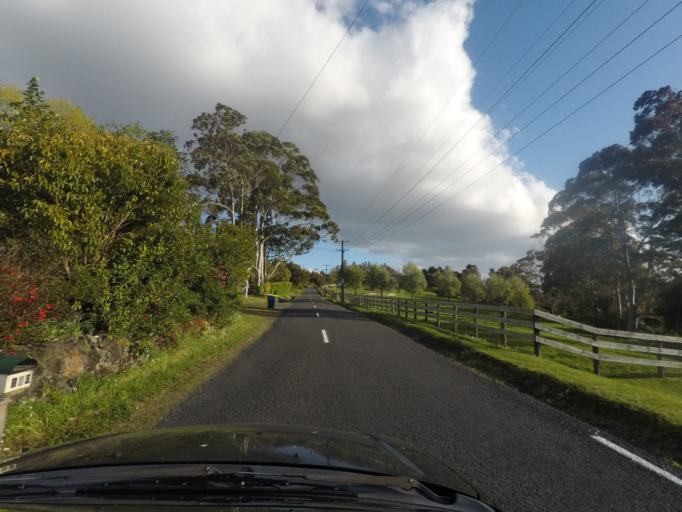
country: NZ
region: Auckland
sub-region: Auckland
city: Titirangi
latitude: -36.9384
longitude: 174.6199
